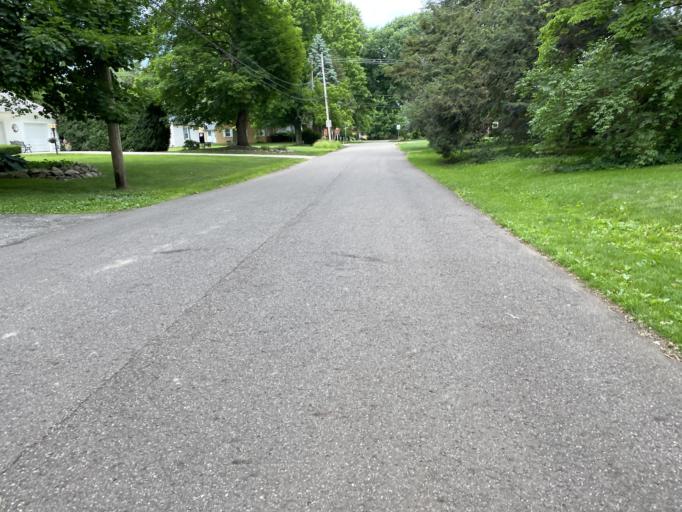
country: US
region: Ohio
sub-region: Summit County
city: Fairlawn
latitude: 41.1133
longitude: -81.5826
